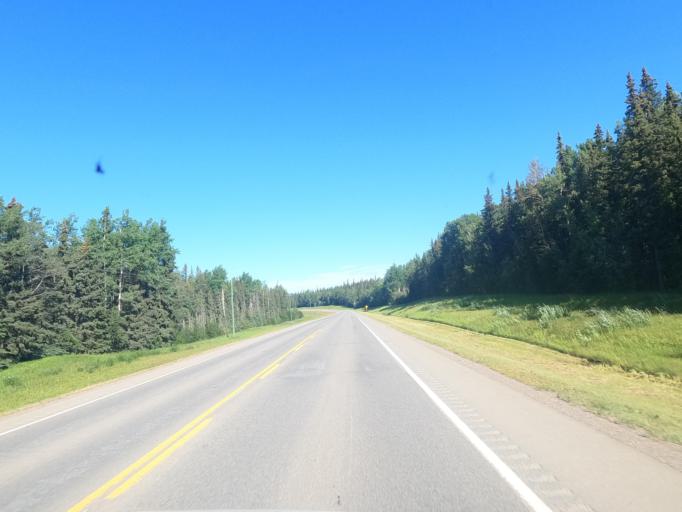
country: CA
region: British Columbia
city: Fort St. John
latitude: 56.6186
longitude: -121.4937
